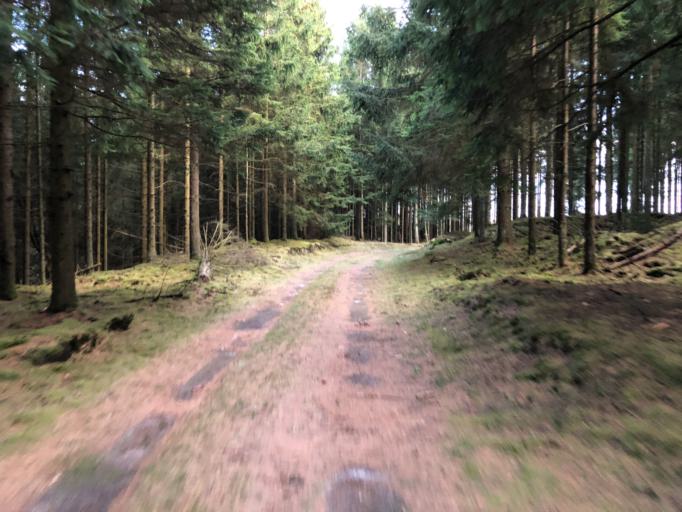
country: DK
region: Central Jutland
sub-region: Holstebro Kommune
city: Ulfborg
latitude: 56.2295
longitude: 8.4255
